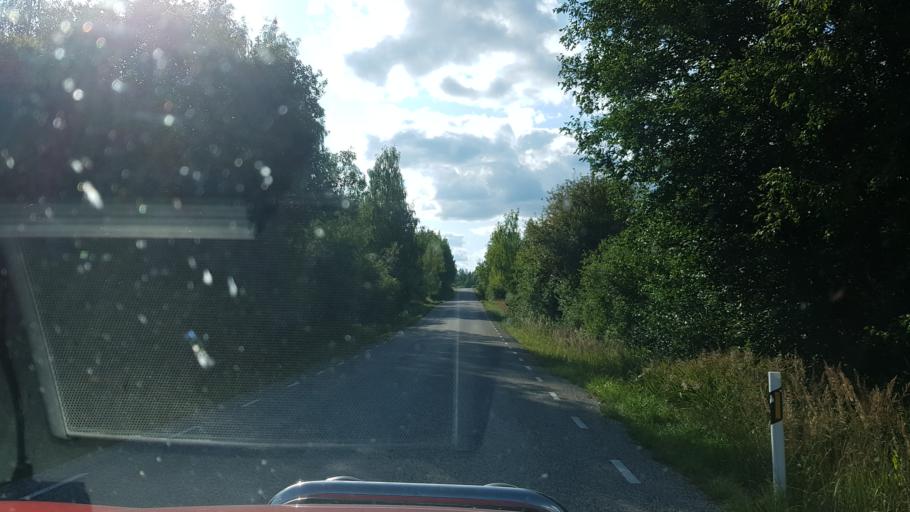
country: EE
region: Vorumaa
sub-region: Voru linn
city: Voru
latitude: 57.9278
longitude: 27.0659
